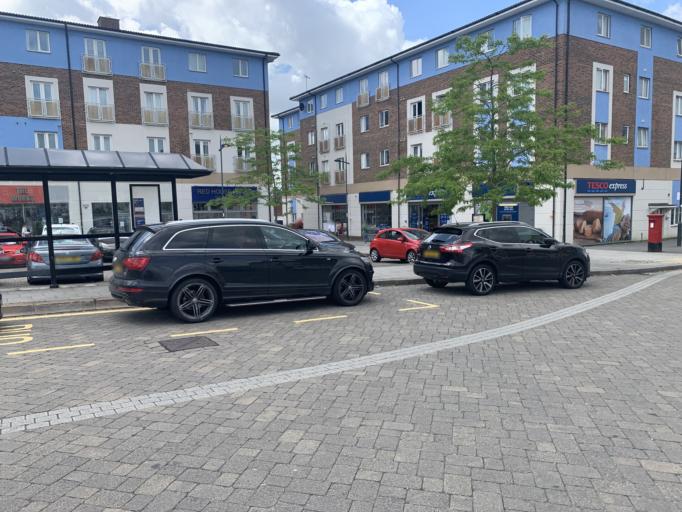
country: GB
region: England
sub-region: Borough of Swindon
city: Broad Blunsdon
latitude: 51.6028
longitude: -1.8160
